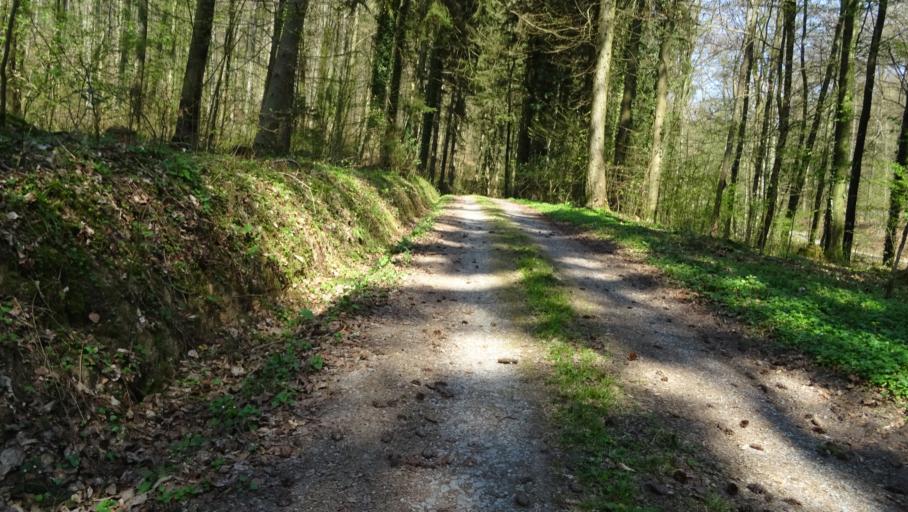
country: DE
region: Baden-Wuerttemberg
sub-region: Karlsruhe Region
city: Obrigheim
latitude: 49.3718
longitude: 9.1019
